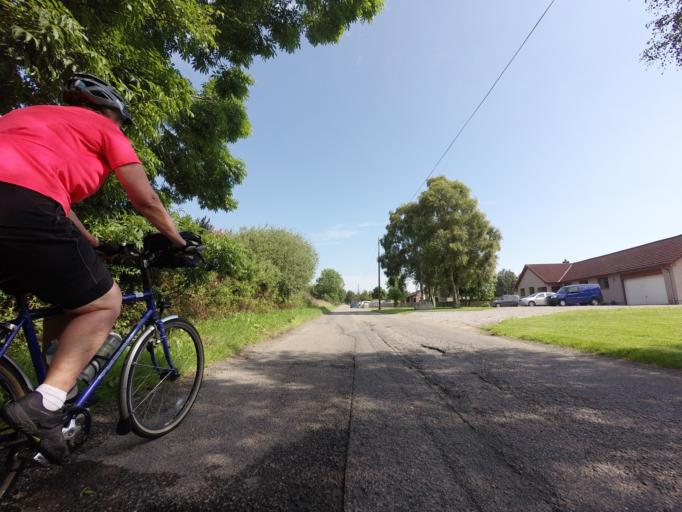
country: GB
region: Scotland
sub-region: Highland
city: Invergordon
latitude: 57.7283
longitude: -4.1946
